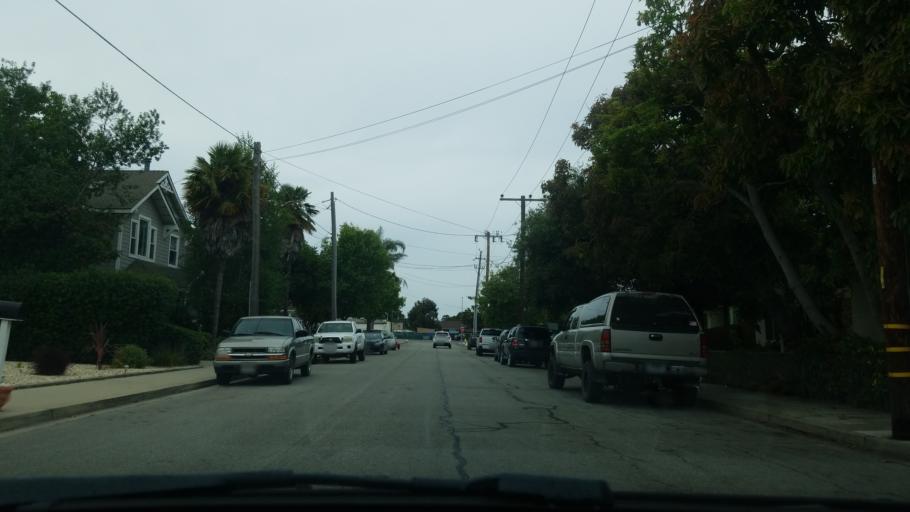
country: US
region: California
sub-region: San Luis Obispo County
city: Arroyo Grande
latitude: 35.1202
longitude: -120.5747
